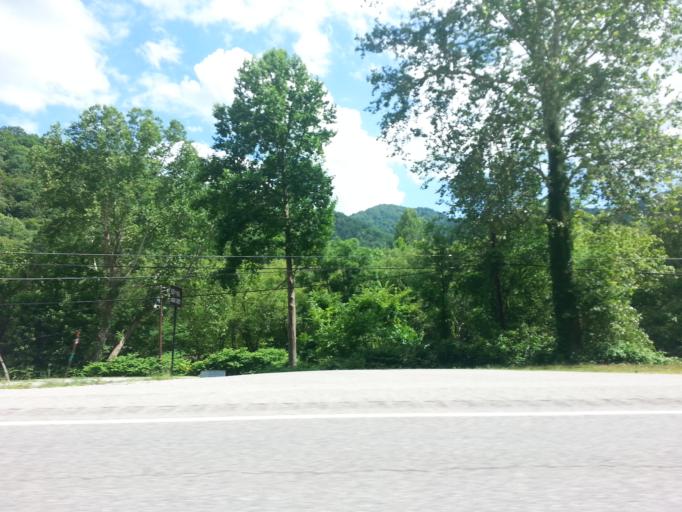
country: US
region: Kentucky
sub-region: Harlan County
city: Harlan
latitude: 36.8093
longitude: -83.2939
